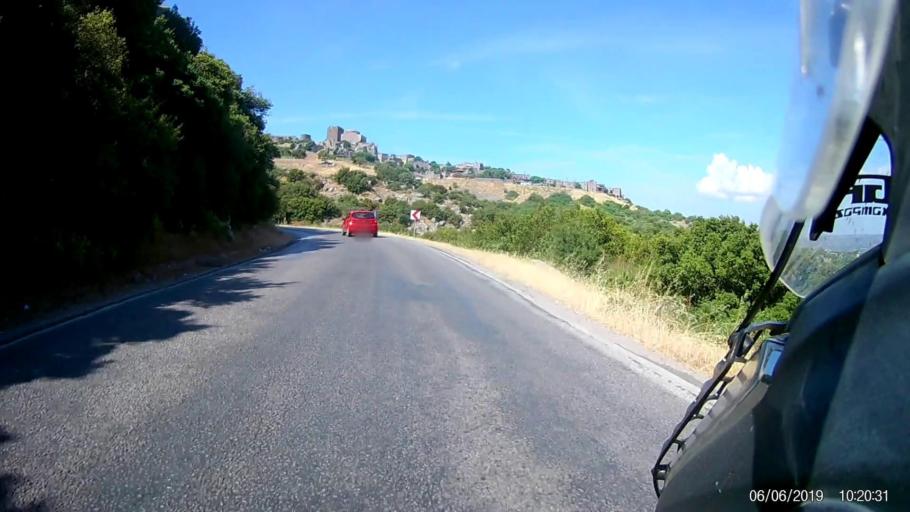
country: TR
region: Canakkale
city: Ayvacik
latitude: 39.5199
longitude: 26.4509
